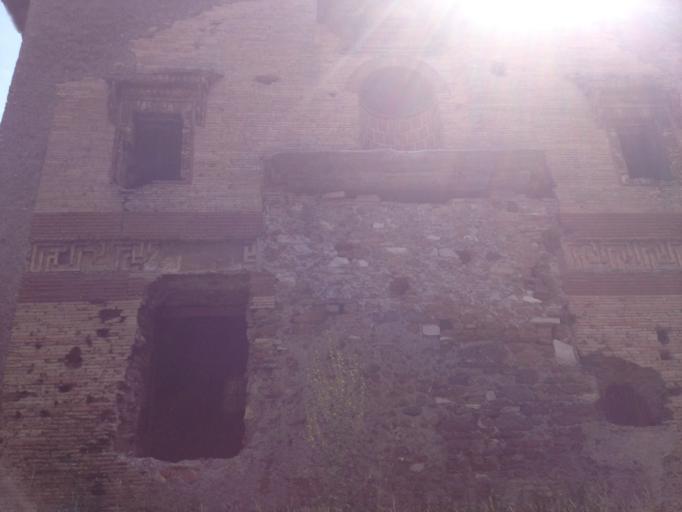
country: IT
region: Latium
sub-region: Citta metropolitana di Roma Capitale
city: Rome
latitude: 41.8652
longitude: 12.5165
